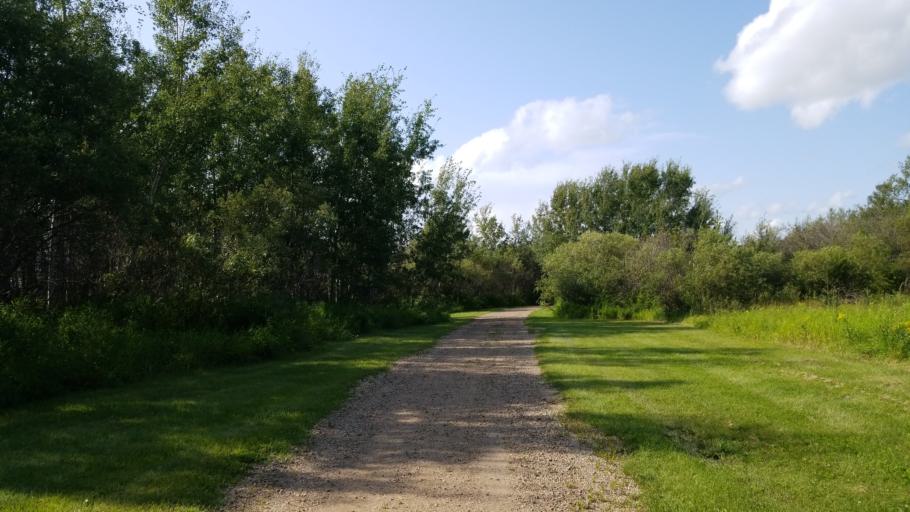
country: CA
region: Saskatchewan
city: Lloydminster
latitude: 53.2572
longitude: -110.0474
